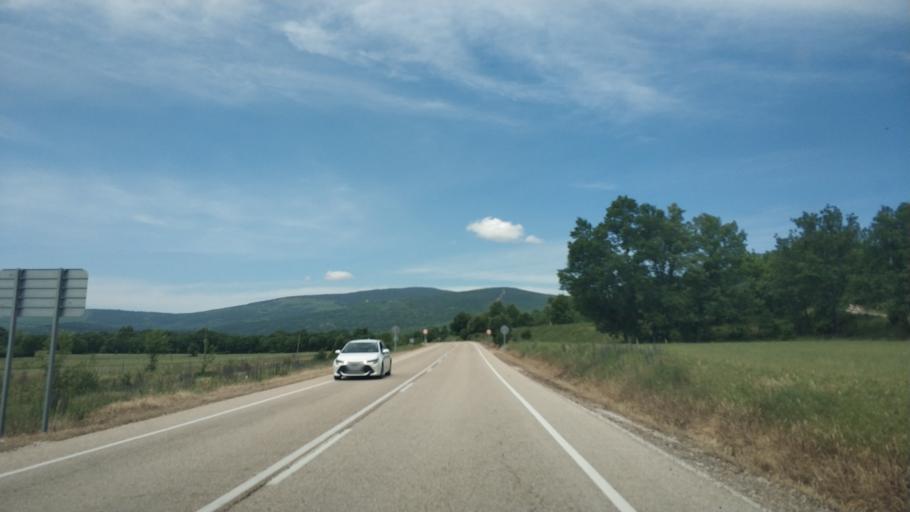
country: ES
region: Castille and Leon
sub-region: Provincia de Soria
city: Sotillo del Rincon
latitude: 41.8910
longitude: -2.6311
